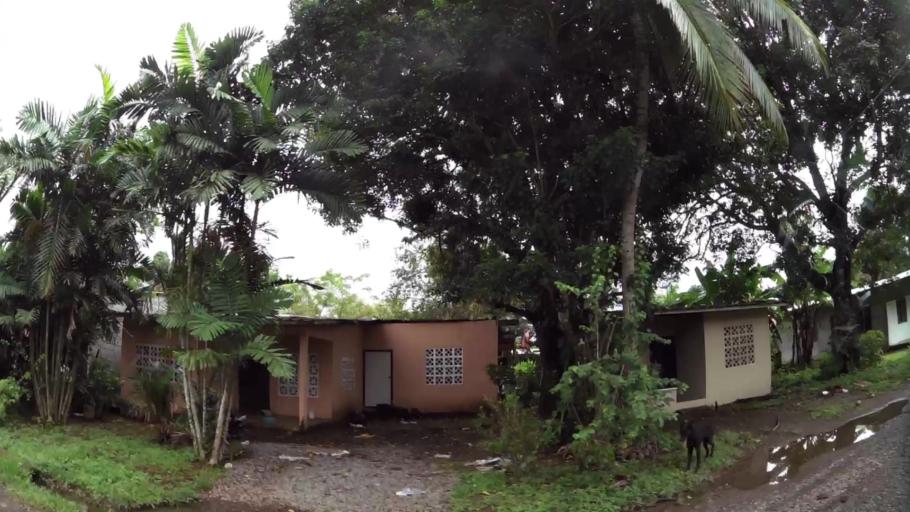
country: PA
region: Chiriqui
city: David
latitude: 8.4161
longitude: -82.4488
